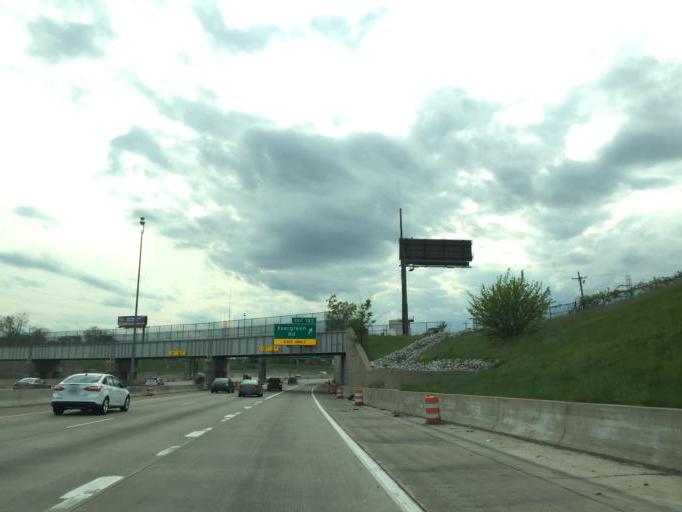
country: US
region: Michigan
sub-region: Wayne County
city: Dearborn Heights
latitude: 42.3782
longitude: -83.2293
